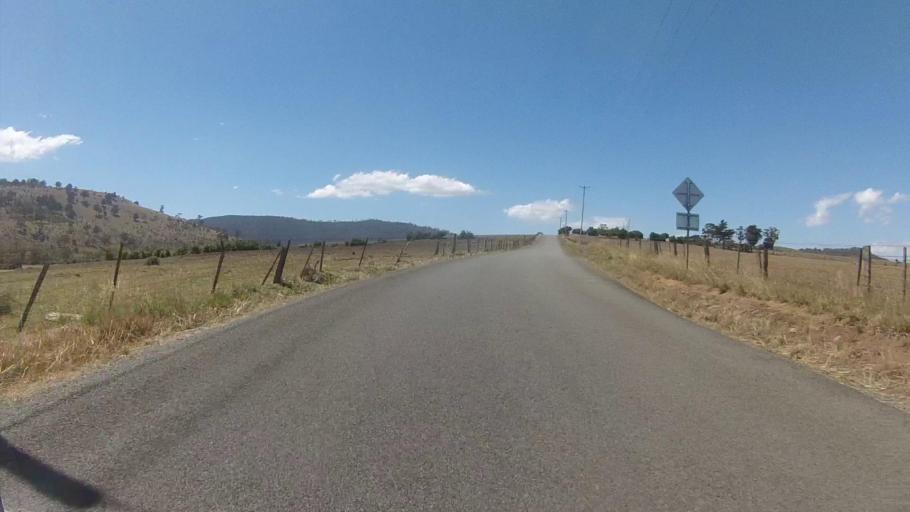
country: AU
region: Tasmania
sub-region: Sorell
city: Sorell
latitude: -42.7691
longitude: 147.5963
